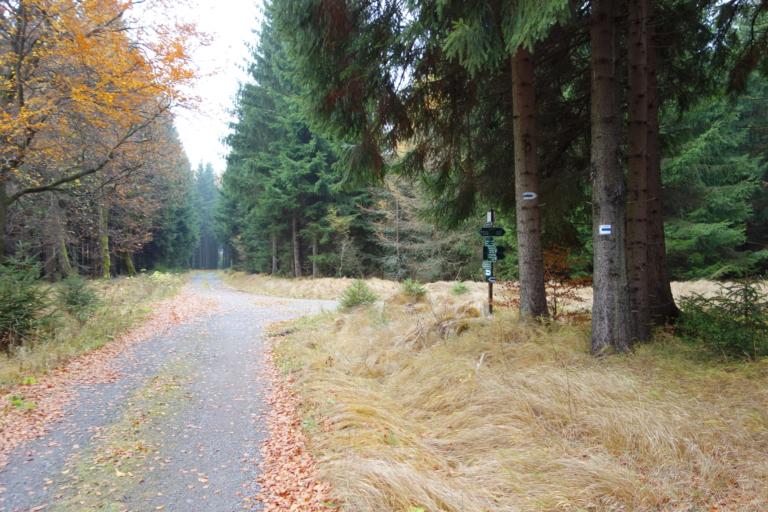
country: DE
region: Saxony
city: Pobershau
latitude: 50.6078
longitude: 13.2762
